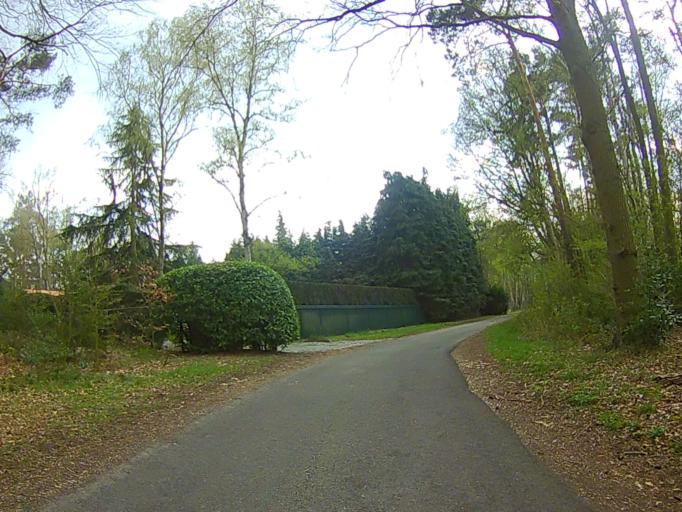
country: BE
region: Flanders
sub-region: Provincie Antwerpen
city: Kapellen
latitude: 51.3284
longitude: 4.4444
